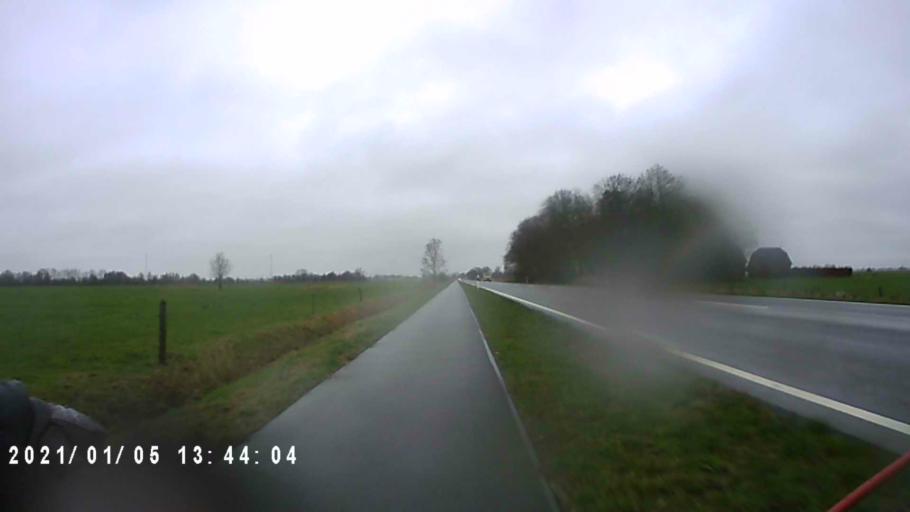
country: DE
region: Lower Saxony
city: Weener
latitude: 53.1935
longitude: 7.3936
